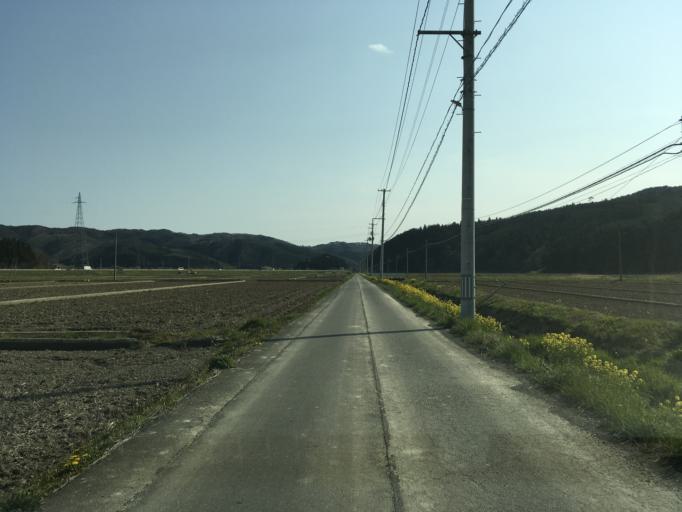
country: JP
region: Iwate
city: Ichinoseki
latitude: 38.7592
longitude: 141.3251
